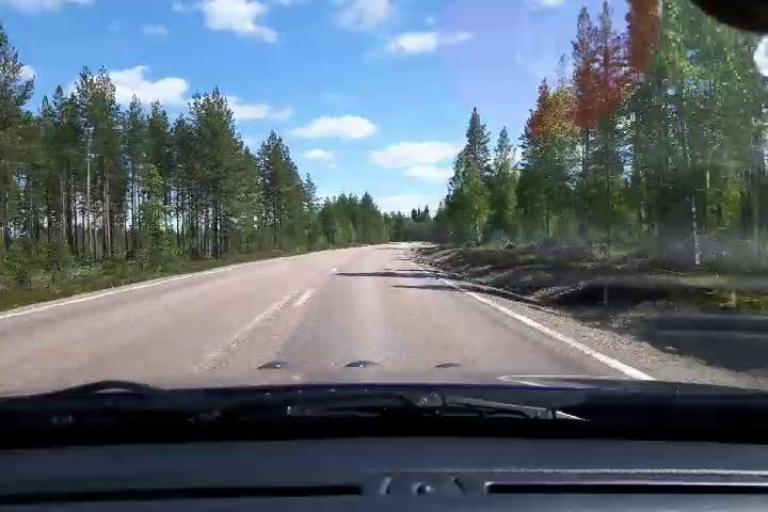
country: SE
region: Gaevleborg
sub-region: Ljusdals Kommun
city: Farila
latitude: 61.9443
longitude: 15.4536
